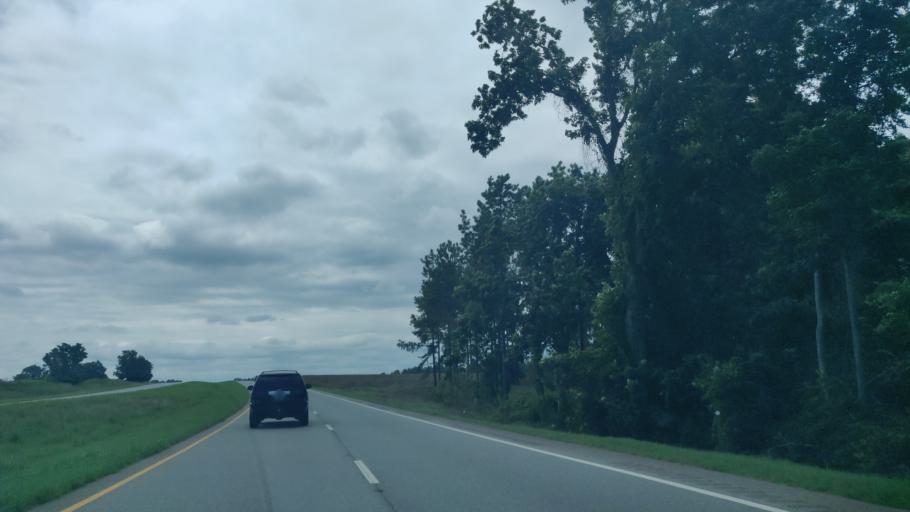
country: US
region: Georgia
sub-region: Terrell County
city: Dawson
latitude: 31.8599
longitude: -84.4824
